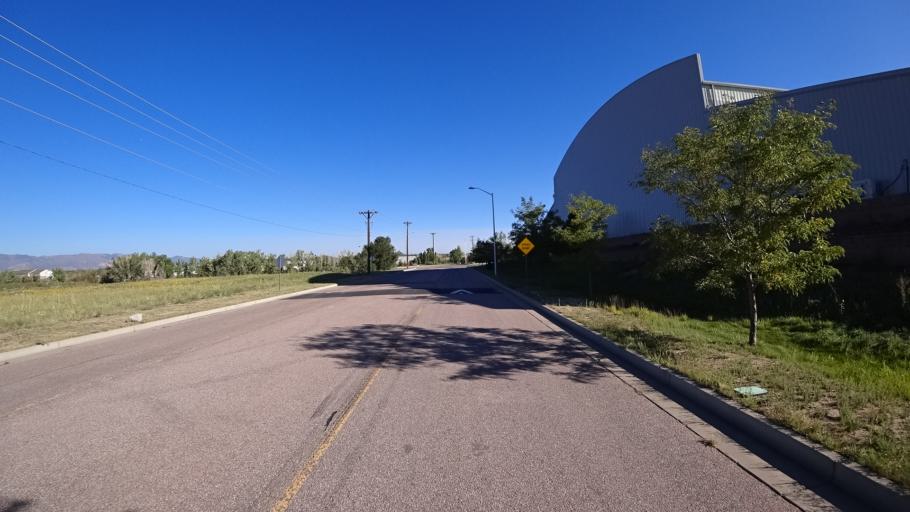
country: US
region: Colorado
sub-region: El Paso County
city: Cimarron Hills
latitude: 38.8209
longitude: -104.7224
